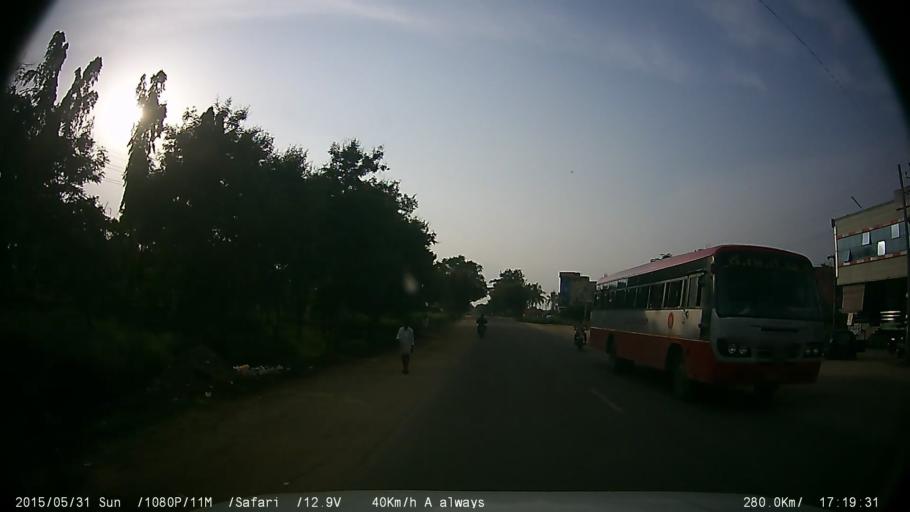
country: IN
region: Karnataka
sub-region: Chamrajnagar
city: Gundlupet
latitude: 11.8161
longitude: 76.6850
